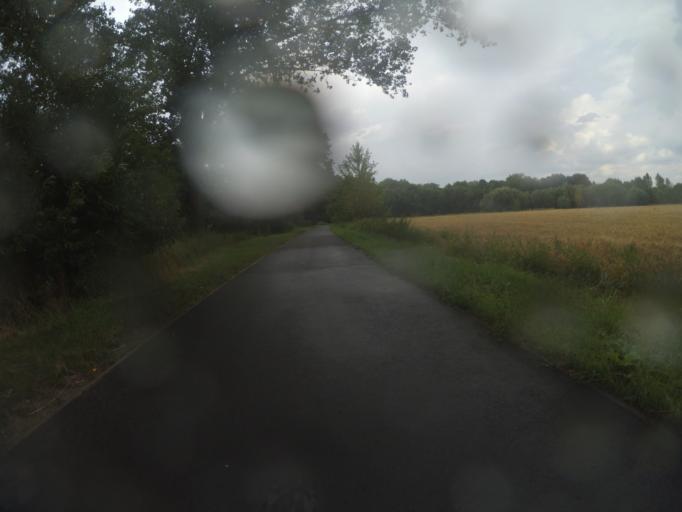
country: CZ
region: Central Bohemia
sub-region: Okres Melnik
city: Melnik
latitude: 50.3366
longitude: 14.4693
